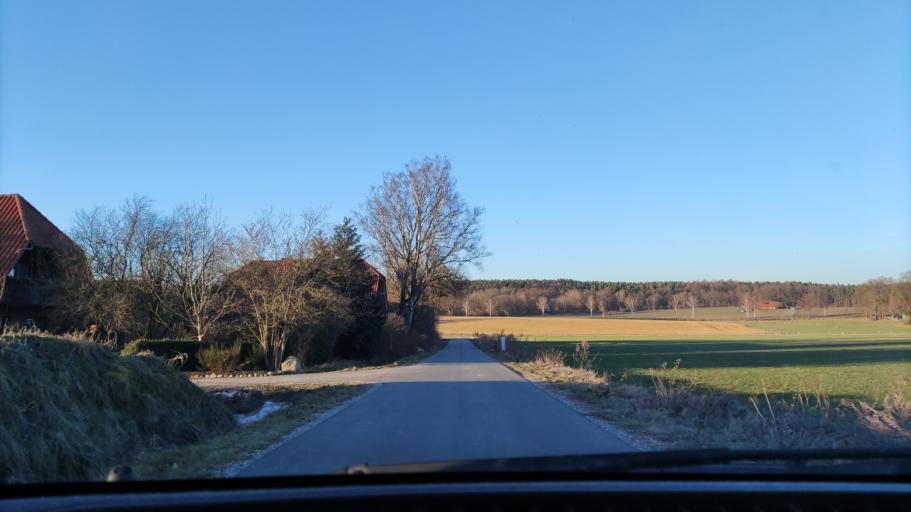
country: DE
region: Lower Saxony
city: Gohrde
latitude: 53.1618
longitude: 10.8550
